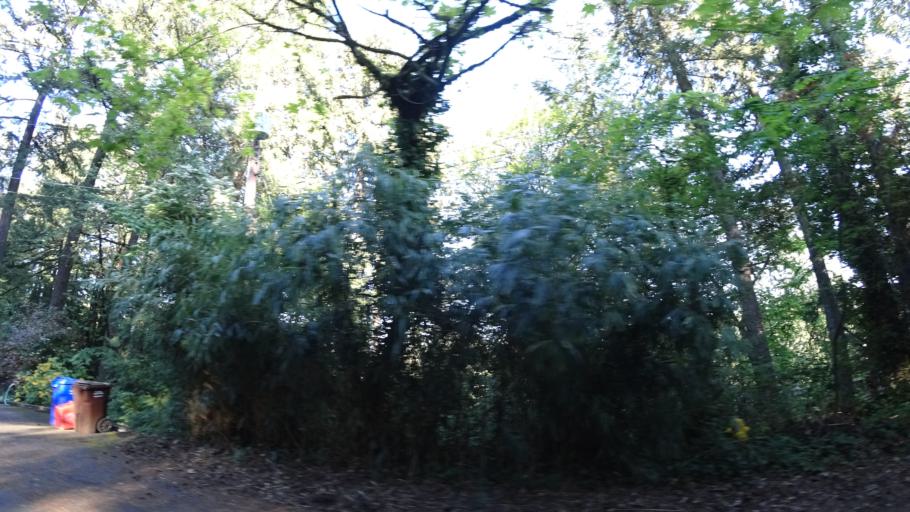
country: US
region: Oregon
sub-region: Washington County
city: West Slope
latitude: 45.4967
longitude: -122.7740
